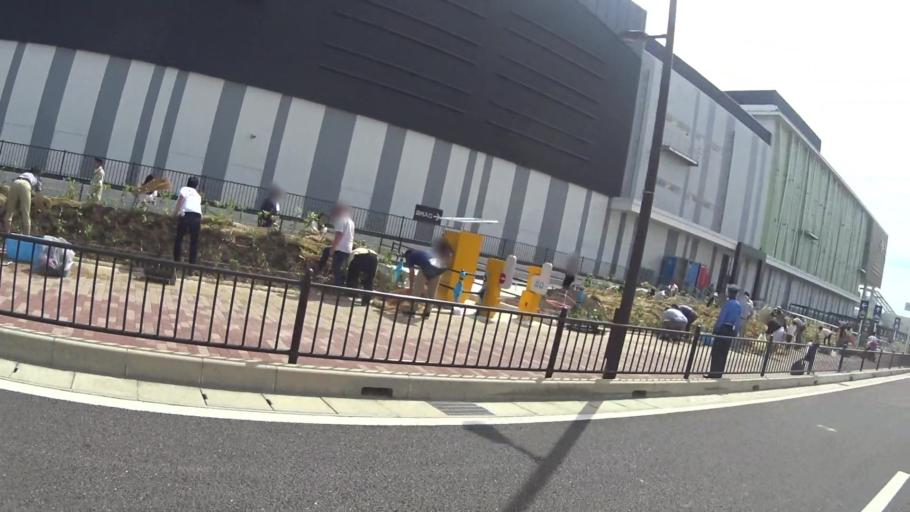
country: JP
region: Kyoto
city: Muko
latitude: 34.9630
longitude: 135.7062
